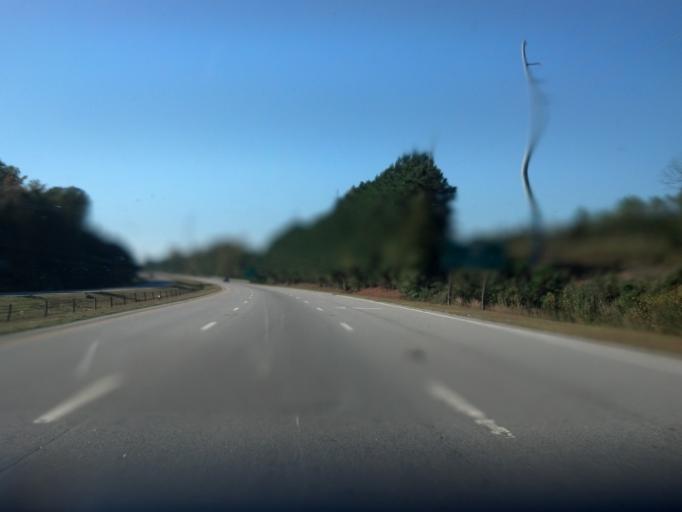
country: US
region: North Carolina
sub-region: Pitt County
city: Summerfield
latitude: 35.6252
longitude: -77.4358
